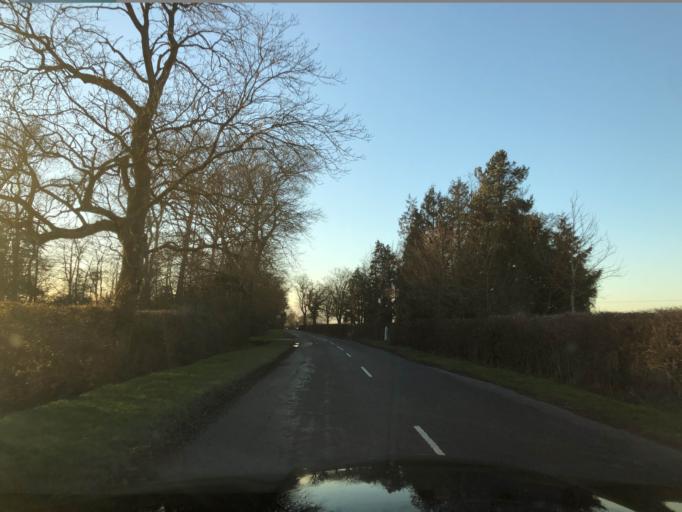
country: GB
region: England
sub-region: Warwickshire
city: Harbury
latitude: 52.2265
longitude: -1.4594
